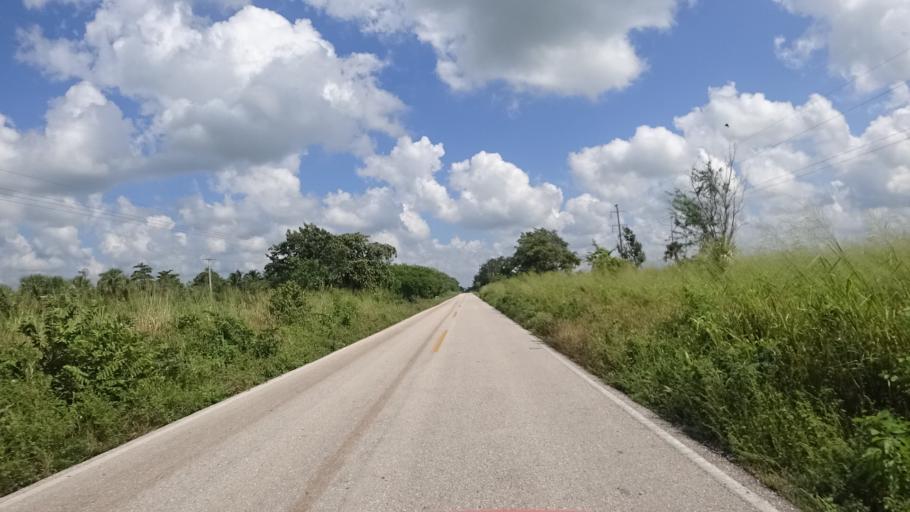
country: MX
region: Yucatan
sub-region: Panaba
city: Loche
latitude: 21.3098
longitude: -88.1647
